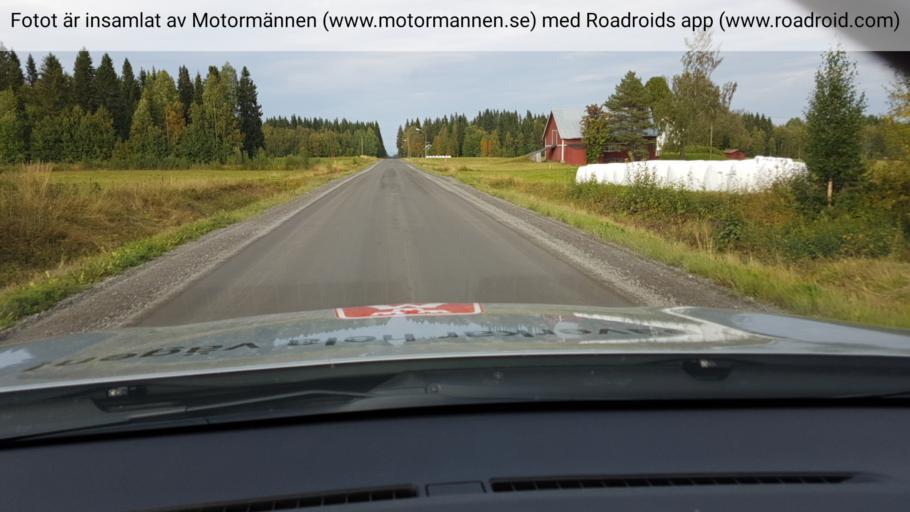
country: SE
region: Jaemtland
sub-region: Stroemsunds Kommun
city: Stroemsund
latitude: 64.0561
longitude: 15.8131
